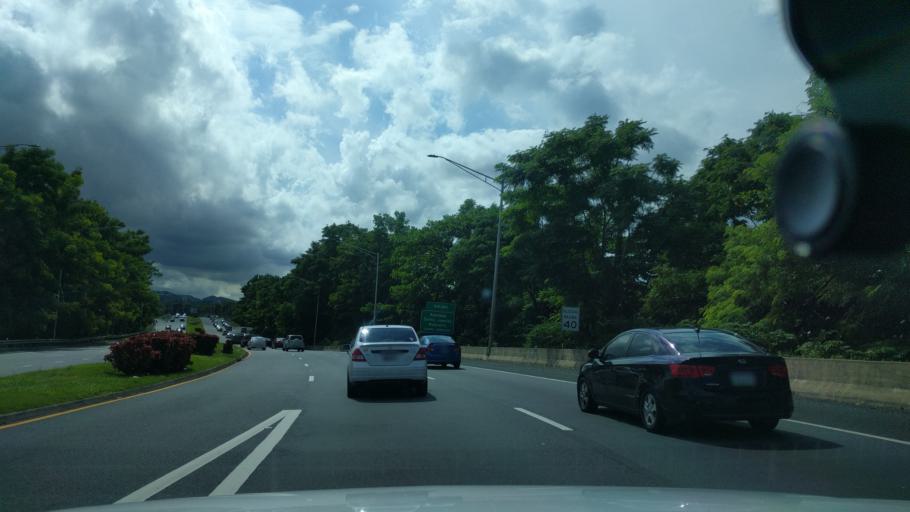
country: PR
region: Bayamon
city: Bayamon
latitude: 18.3732
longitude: -66.1647
